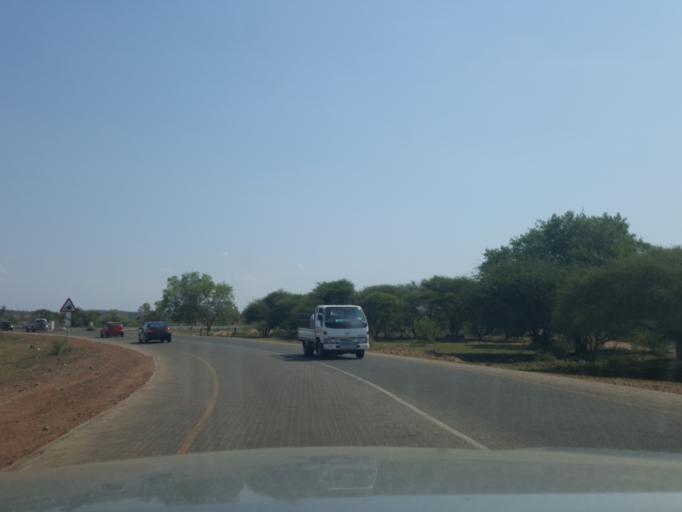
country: BW
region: South East
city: Ramotswa
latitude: -24.8517
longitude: 25.8284
